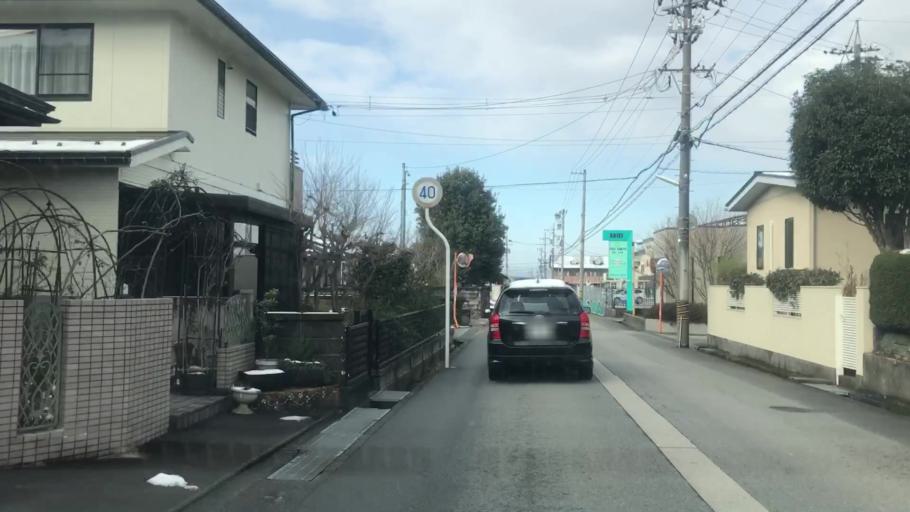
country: JP
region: Toyama
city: Toyama-shi
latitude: 36.6506
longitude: 137.2223
